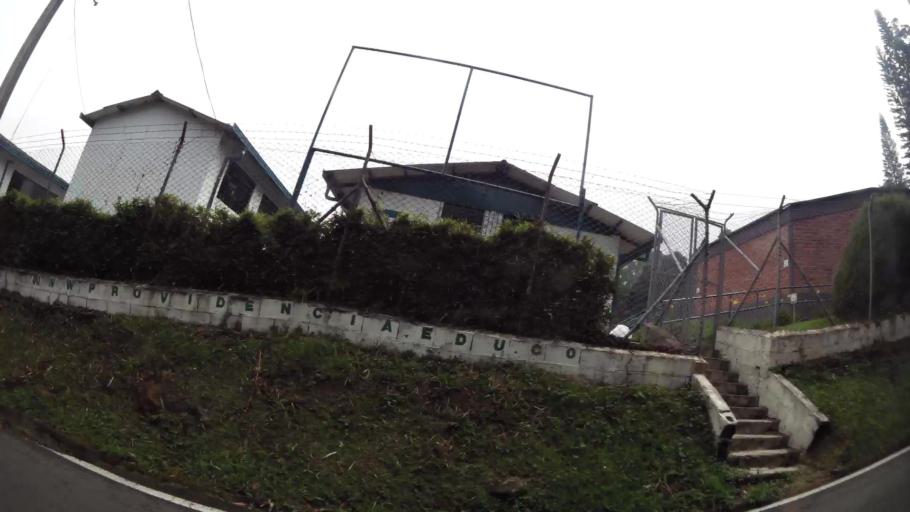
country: CO
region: Antioquia
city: Medellin
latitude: 6.2054
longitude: -75.5497
